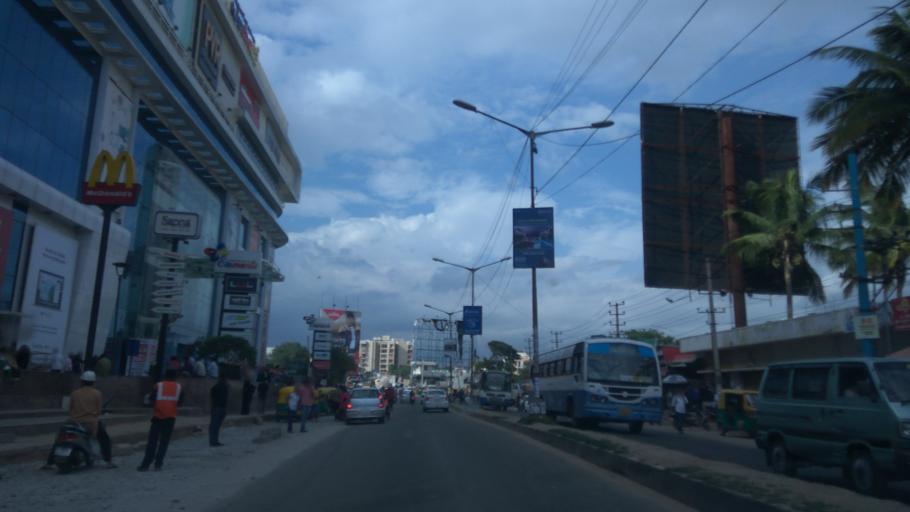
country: IN
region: Karnataka
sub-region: Bangalore Urban
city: Yelahanka
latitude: 13.0446
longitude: 77.6266
